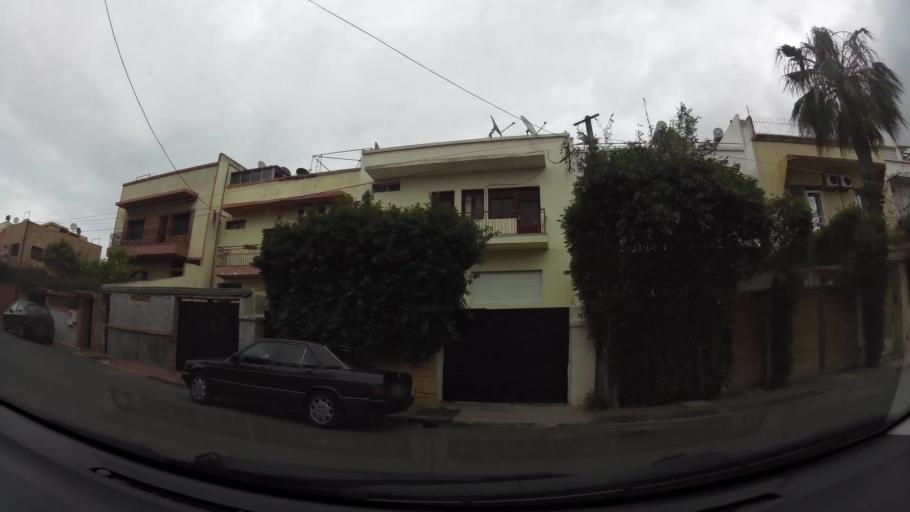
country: MA
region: Grand Casablanca
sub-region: Casablanca
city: Casablanca
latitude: 33.5734
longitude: -7.6690
